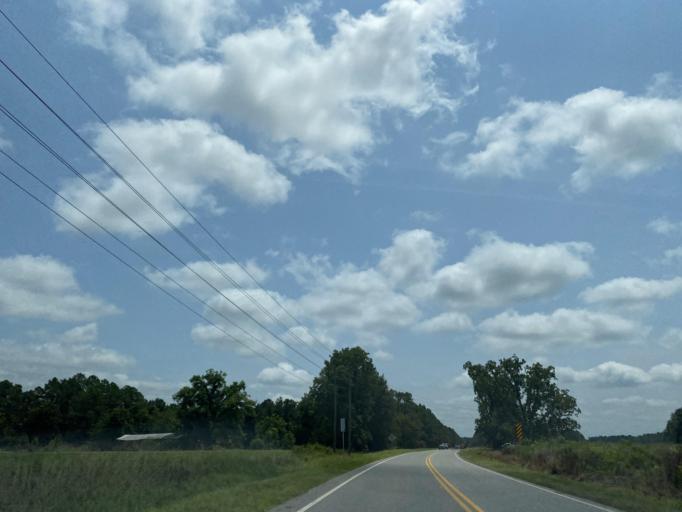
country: US
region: Georgia
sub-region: Jeff Davis County
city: Hazlehurst
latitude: 31.8061
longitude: -82.5655
